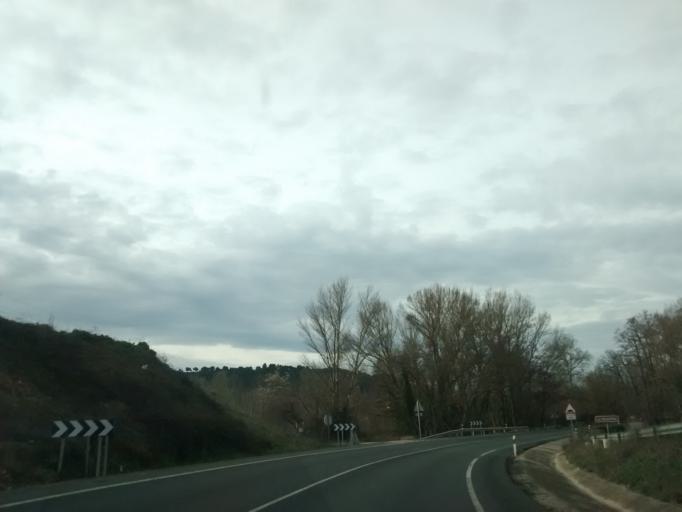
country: ES
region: La Rioja
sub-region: Provincia de La Rioja
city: Torremontalbo
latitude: 42.4972
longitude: -2.6831
